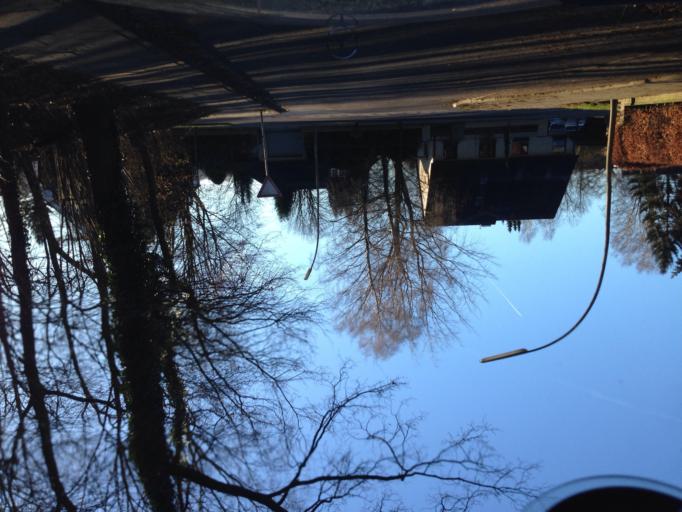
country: DE
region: Schleswig-Holstein
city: Barsbuettel
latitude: 53.5890
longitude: 10.1741
